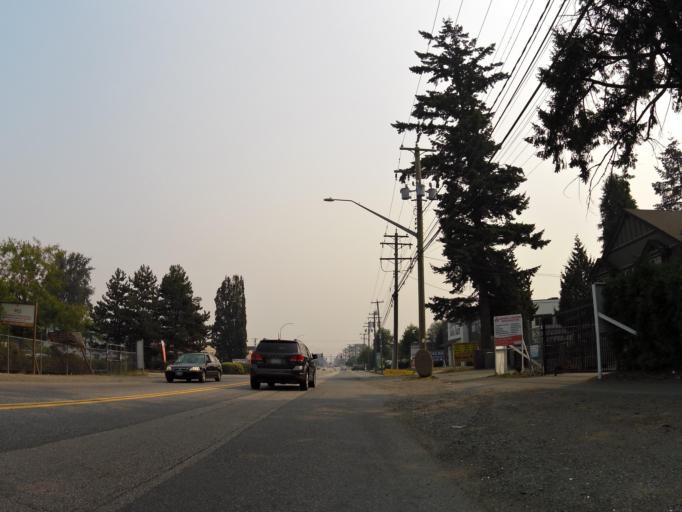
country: CA
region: British Columbia
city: Delta
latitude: 49.1482
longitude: -122.8707
